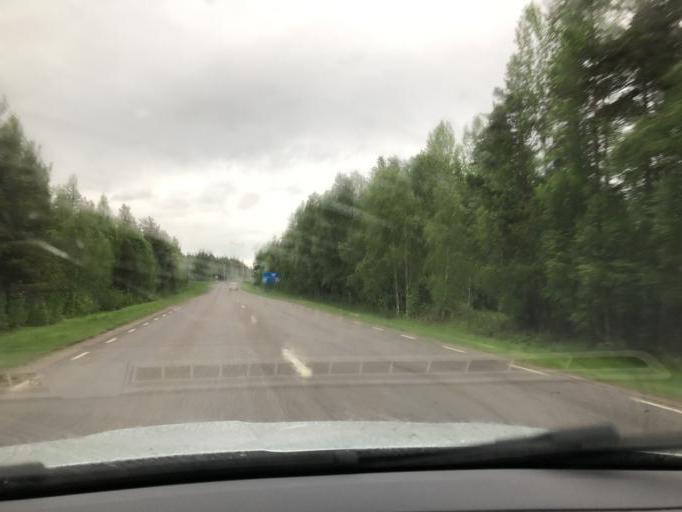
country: SE
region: Norrbotten
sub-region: Pitea Kommun
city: Bergsviken
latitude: 65.3327
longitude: 21.4200
